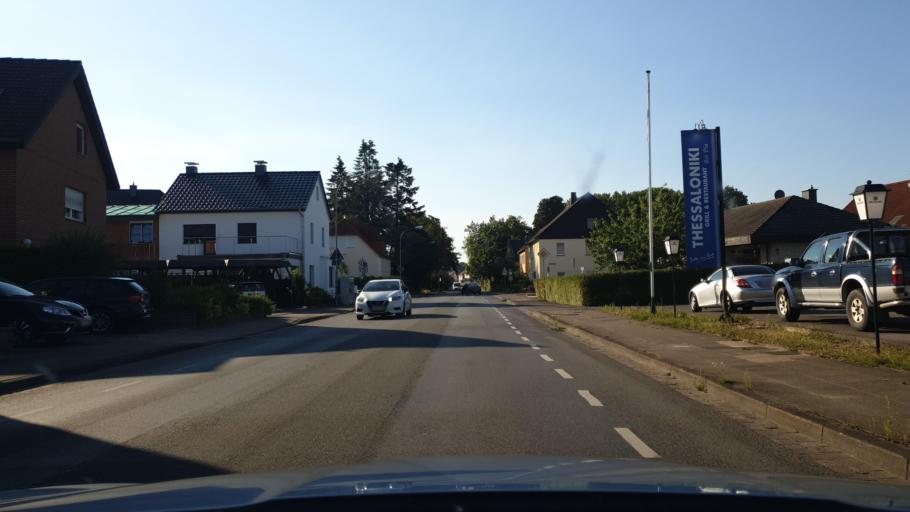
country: DE
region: North Rhine-Westphalia
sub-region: Regierungsbezirk Detmold
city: Bad Salzuflen
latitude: 52.0626
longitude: 8.7731
